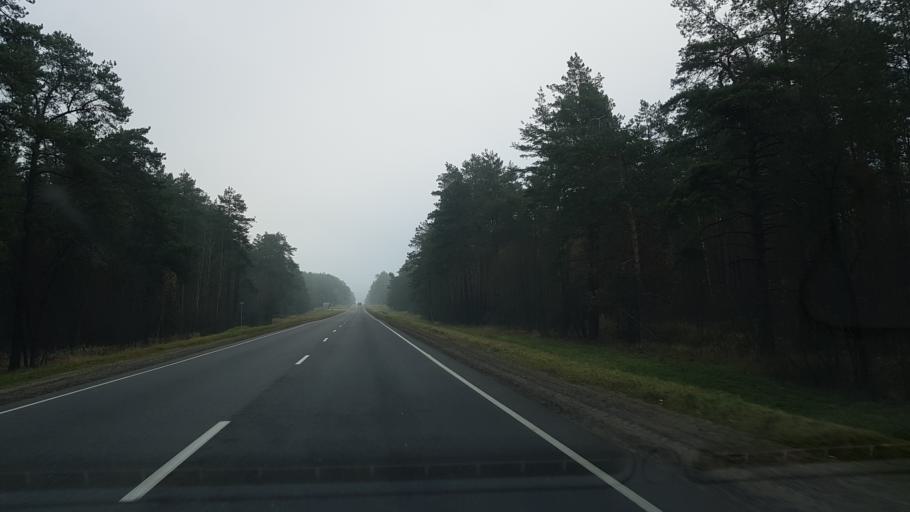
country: BY
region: Mogilev
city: Babruysk
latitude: 53.1588
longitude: 29.3200
